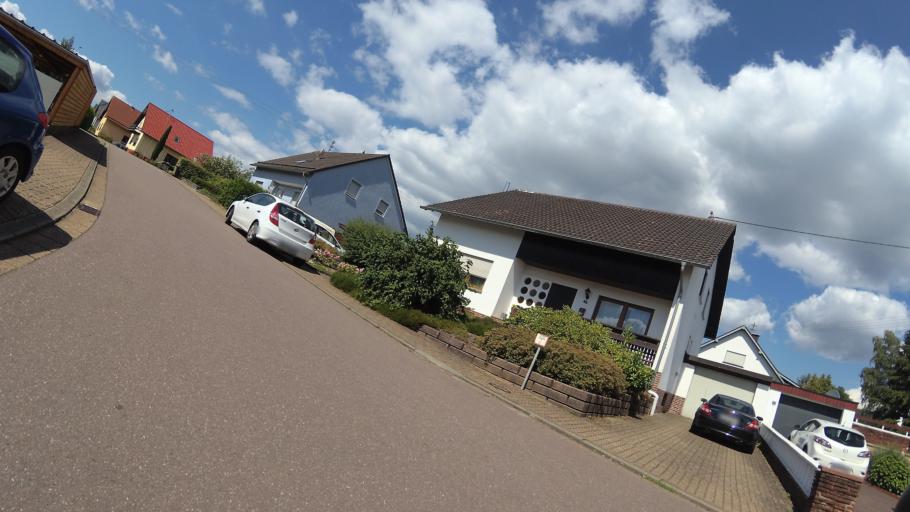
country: DE
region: Saarland
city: Weiskirchen
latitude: 49.5456
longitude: 6.7885
